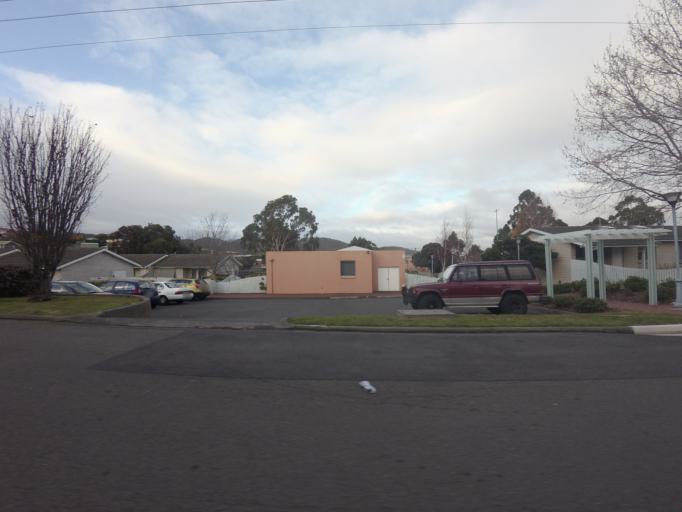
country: AU
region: Tasmania
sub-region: Clarence
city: Rokeby
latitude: -42.8947
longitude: 147.4299
